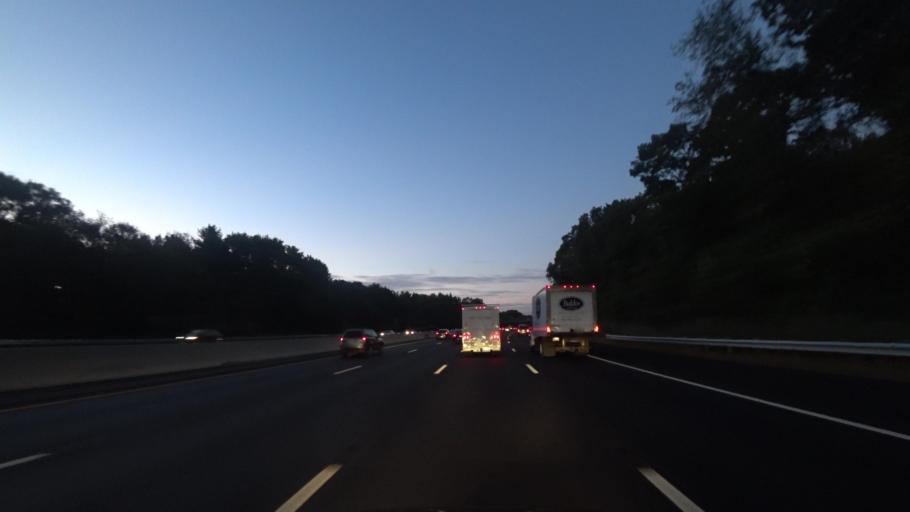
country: US
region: Massachusetts
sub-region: Middlesex County
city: Lexington
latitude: 42.4502
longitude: -71.2557
